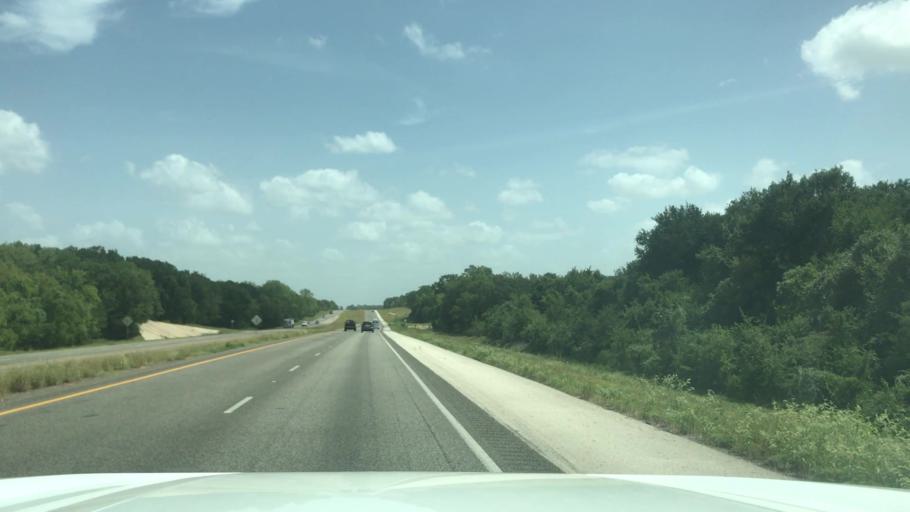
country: US
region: Texas
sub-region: Robertson County
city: Calvert
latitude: 30.9457
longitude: -96.6467
